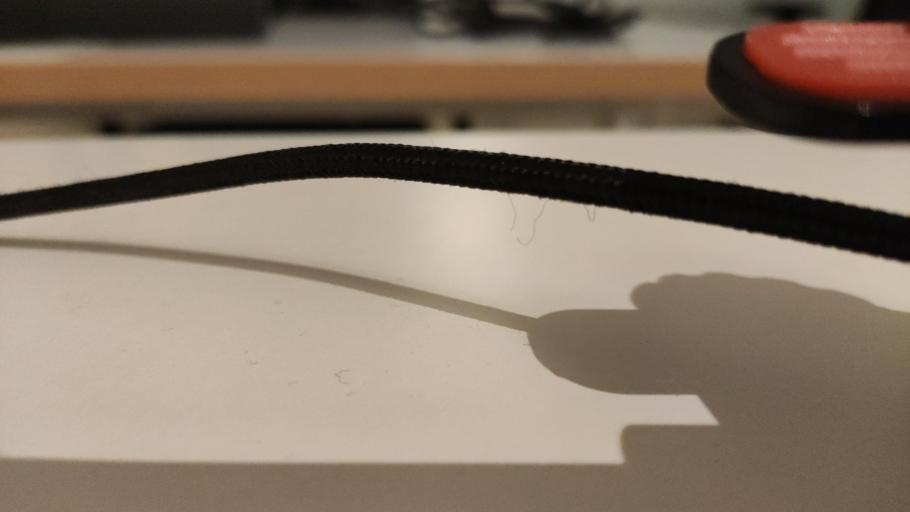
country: RU
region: Moskovskaya
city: Novoye
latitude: 55.6073
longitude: 38.9278
